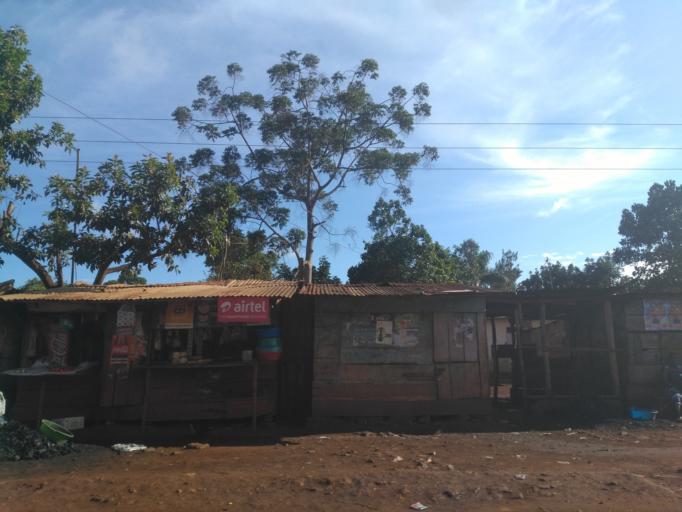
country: UG
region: Eastern Region
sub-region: Jinja District
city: Jinja
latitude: 0.4533
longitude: 33.1894
